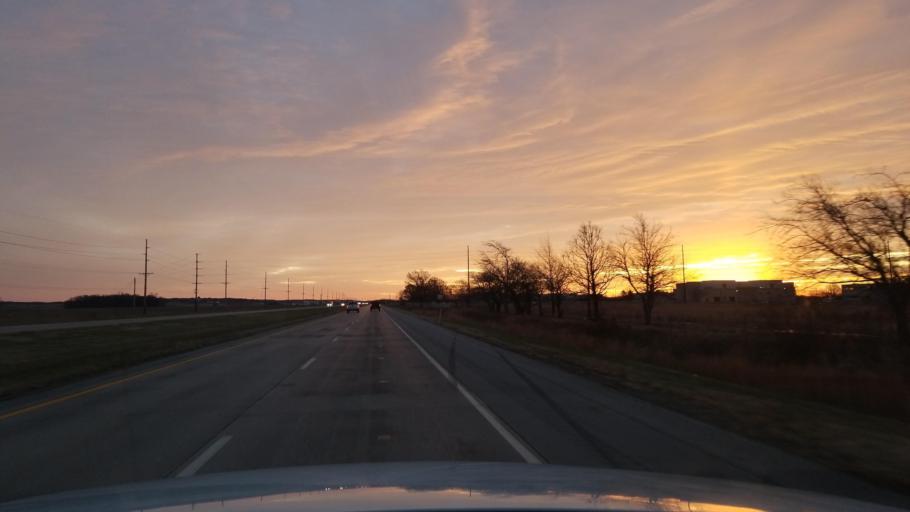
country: US
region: Indiana
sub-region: Posey County
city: Mount Vernon
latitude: 37.9427
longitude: -87.8480
